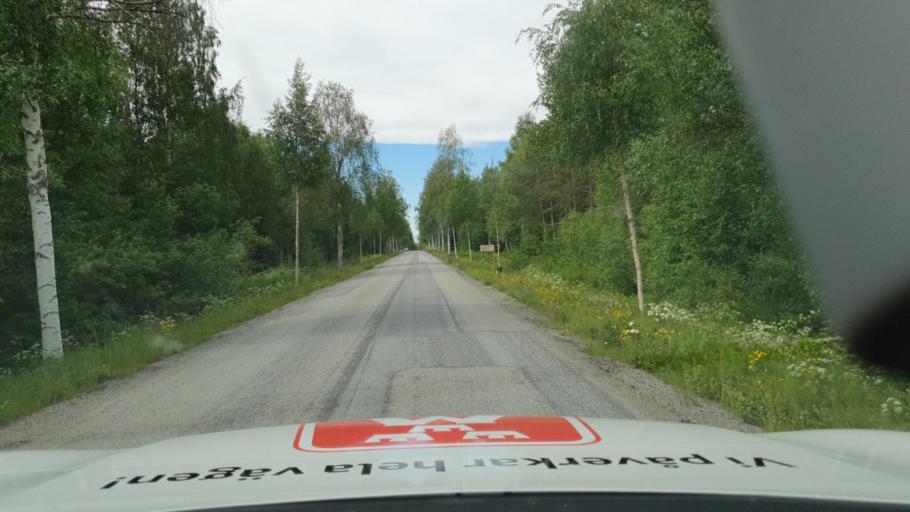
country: SE
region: Vaesterbotten
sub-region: Skelleftea Kommun
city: Burtraesk
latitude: 64.4391
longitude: 20.4968
